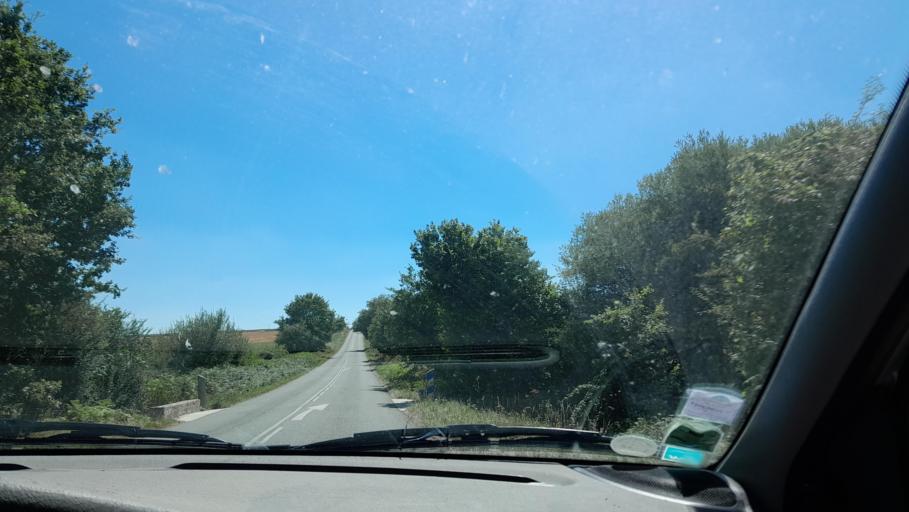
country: FR
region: Pays de la Loire
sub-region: Departement de la Mayenne
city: Congrier
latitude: 47.8649
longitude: -1.1316
